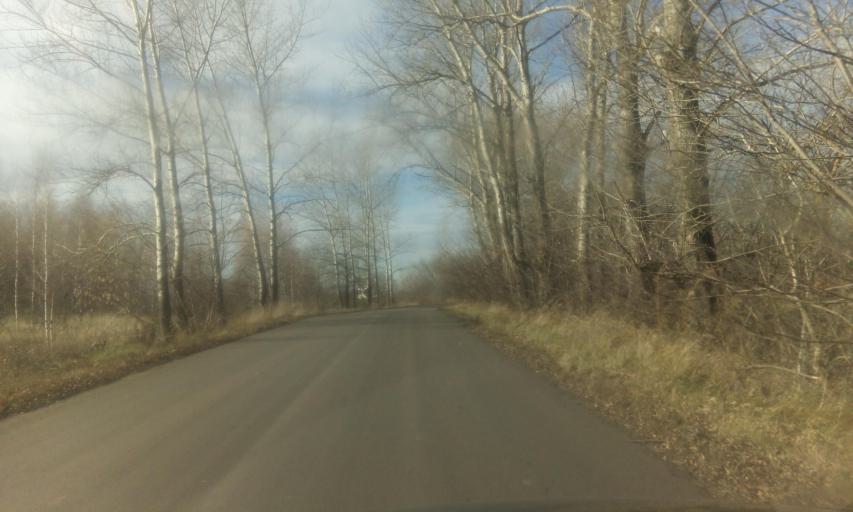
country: RU
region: Tula
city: Dubovka
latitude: 53.9578
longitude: 38.0551
